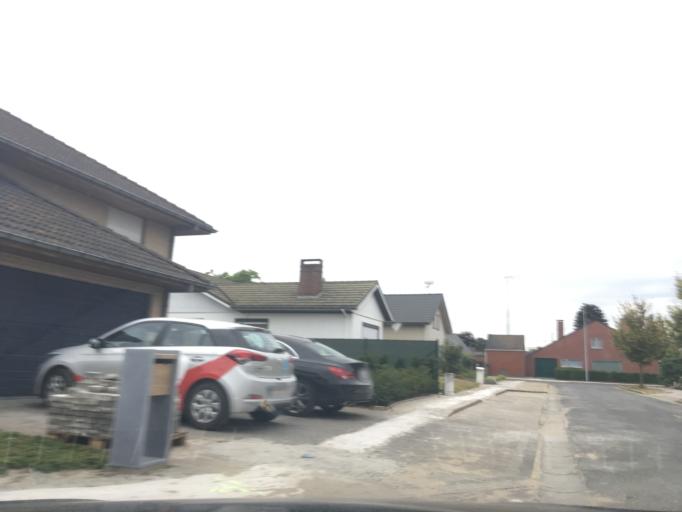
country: BE
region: Flanders
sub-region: Provincie West-Vlaanderen
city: Izegem
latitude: 50.9333
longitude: 3.2015
